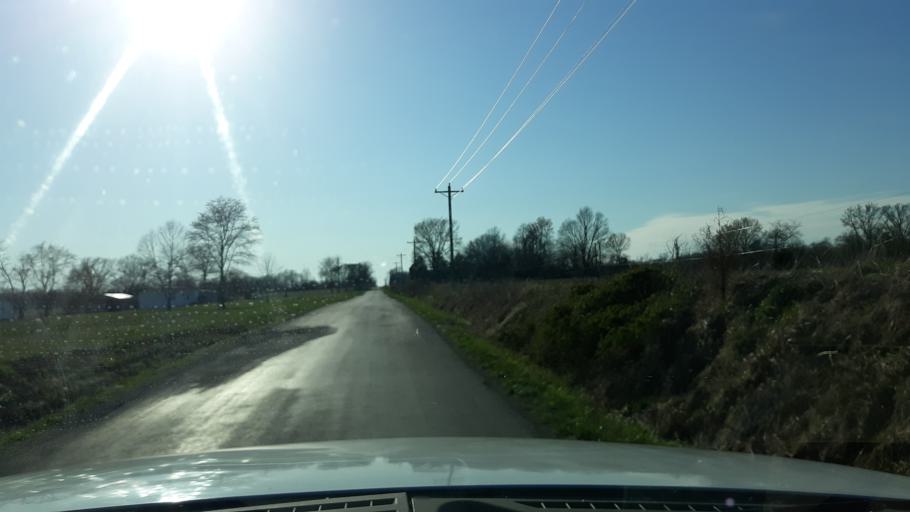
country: US
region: Illinois
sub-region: Saline County
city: Harrisburg
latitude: 37.8049
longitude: -88.6064
